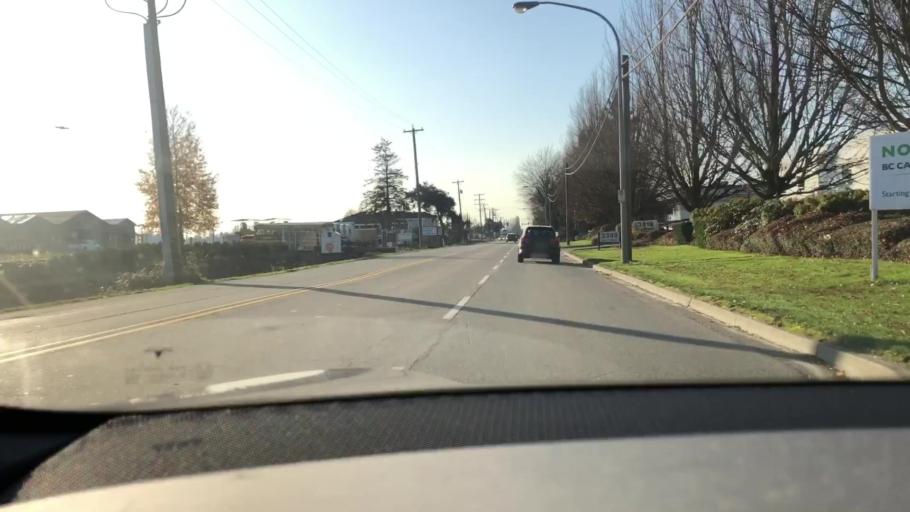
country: CA
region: British Columbia
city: Richmond
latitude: 49.1879
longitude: -123.0692
